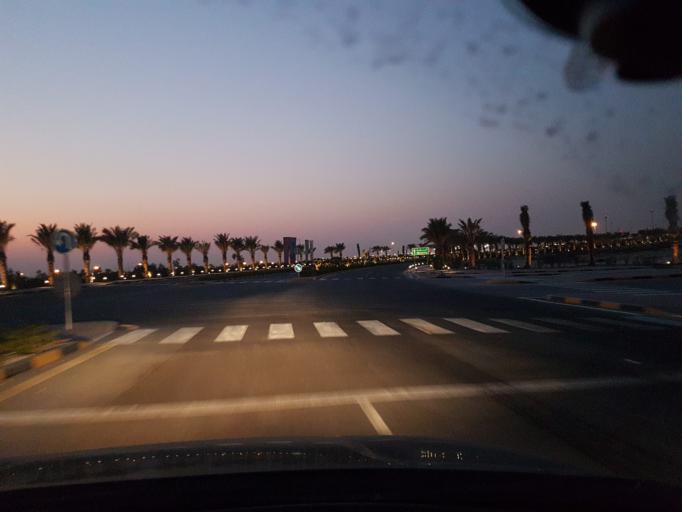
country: BH
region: Central Governorate
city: Dar Kulayb
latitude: 26.0164
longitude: 50.5092
